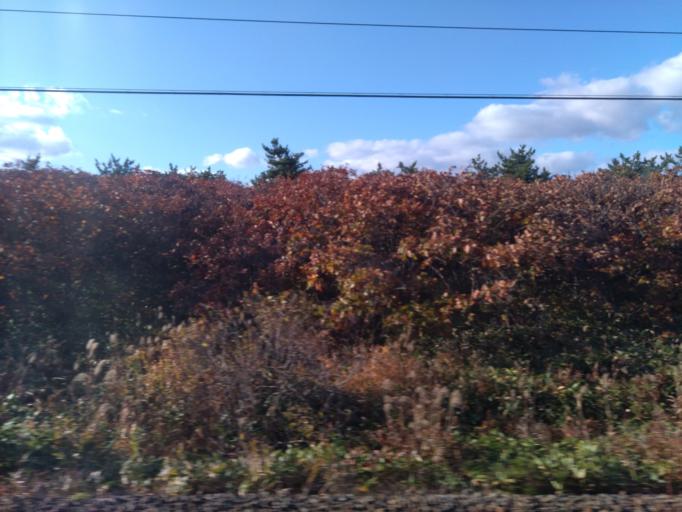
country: JP
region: Hokkaido
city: Niseko Town
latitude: 42.5582
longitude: 140.4270
